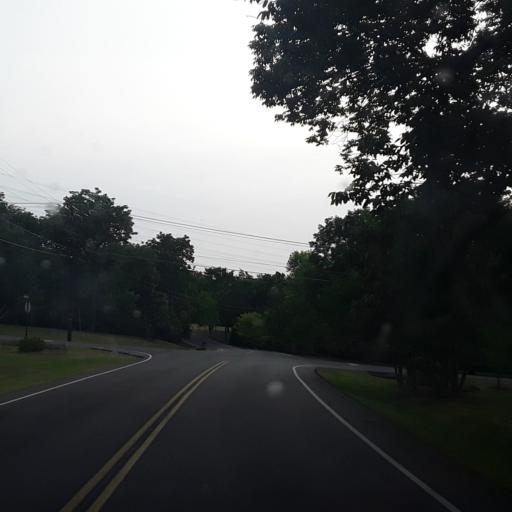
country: US
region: Tennessee
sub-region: Williamson County
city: Brentwood
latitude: 36.0539
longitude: -86.7803
